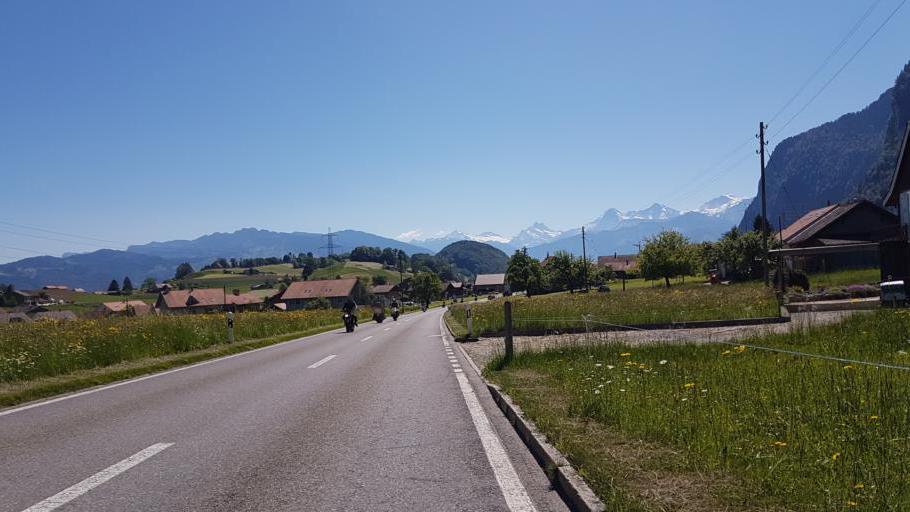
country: CH
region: Bern
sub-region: Thun District
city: Blumenstein
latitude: 46.7182
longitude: 7.5507
